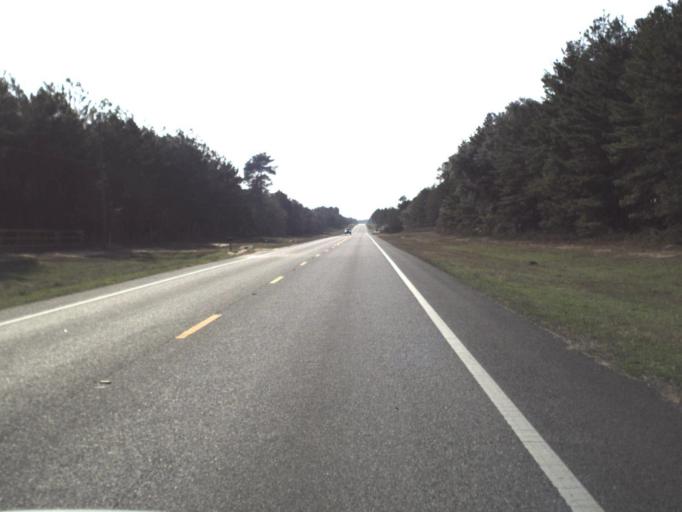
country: US
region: Florida
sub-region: Bay County
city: Lynn Haven
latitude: 30.4267
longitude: -85.6205
